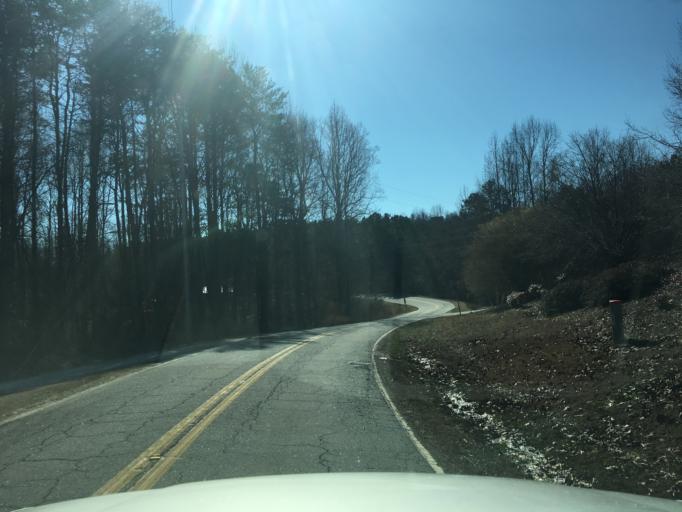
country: US
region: South Carolina
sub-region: Pickens County
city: Pickens
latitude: 34.8360
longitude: -82.7897
